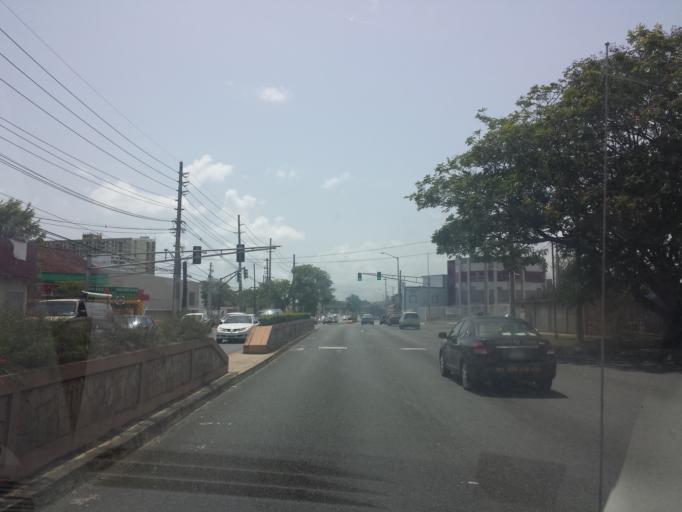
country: PR
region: Bayamon
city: Bayamon
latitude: 18.3957
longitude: -66.1494
